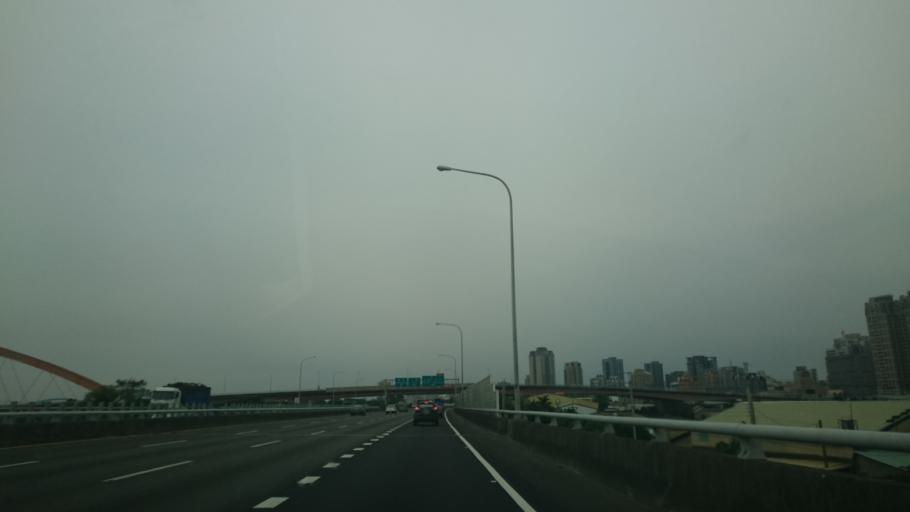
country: TW
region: Taiwan
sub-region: Taichung City
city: Taichung
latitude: 24.1697
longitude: 120.6264
